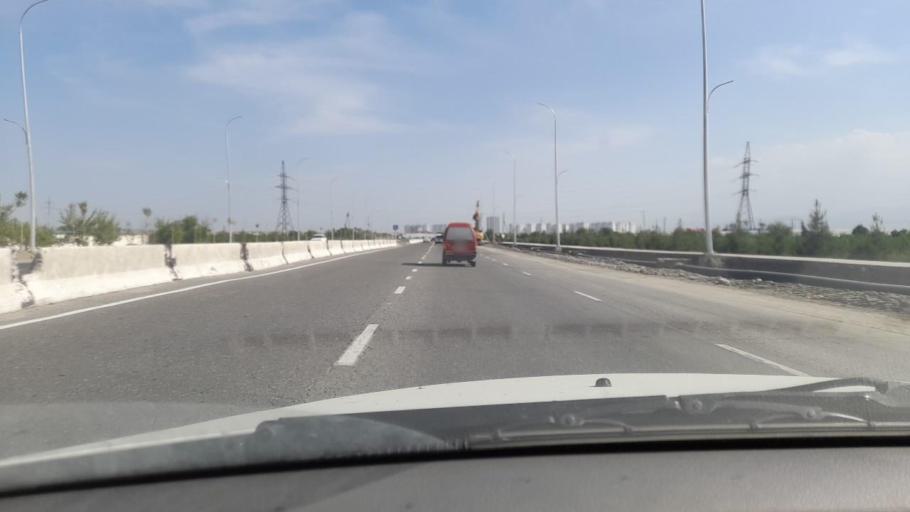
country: UZ
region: Samarqand
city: Daxbet
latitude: 39.7427
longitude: 66.9257
